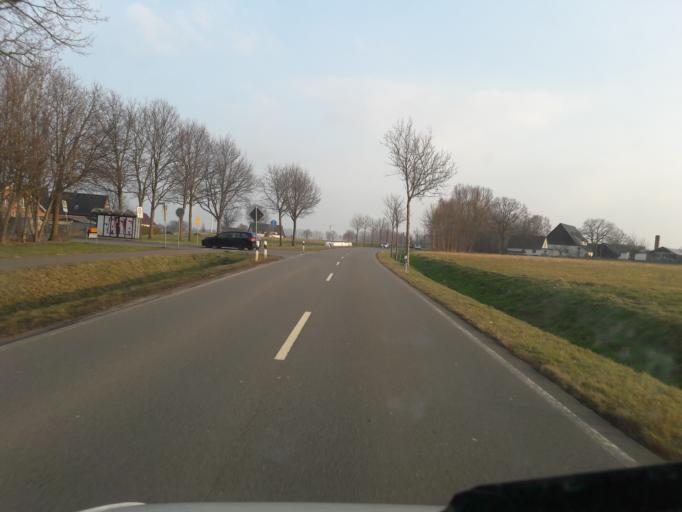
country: DE
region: North Rhine-Westphalia
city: Espelkamp
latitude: 52.3621
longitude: 8.6426
